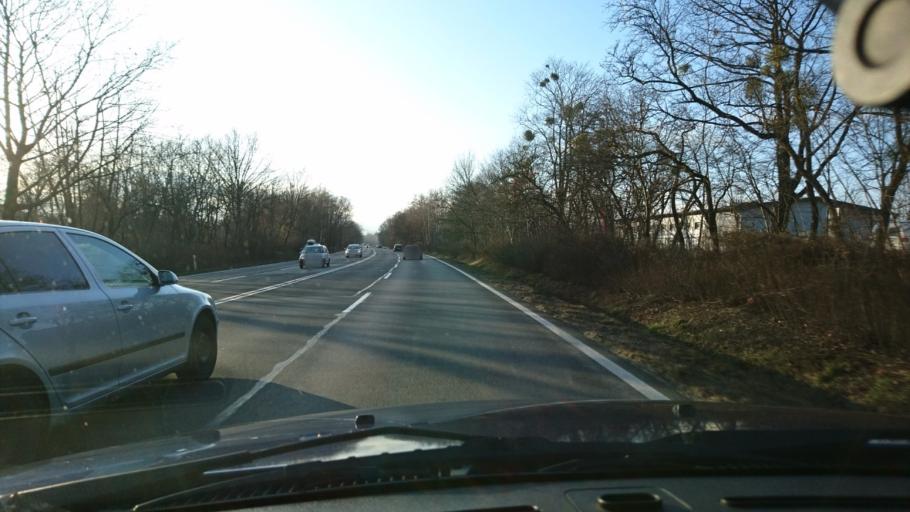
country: PL
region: Silesian Voivodeship
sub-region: Gliwice
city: Gliwice
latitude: 50.3162
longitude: 18.6862
